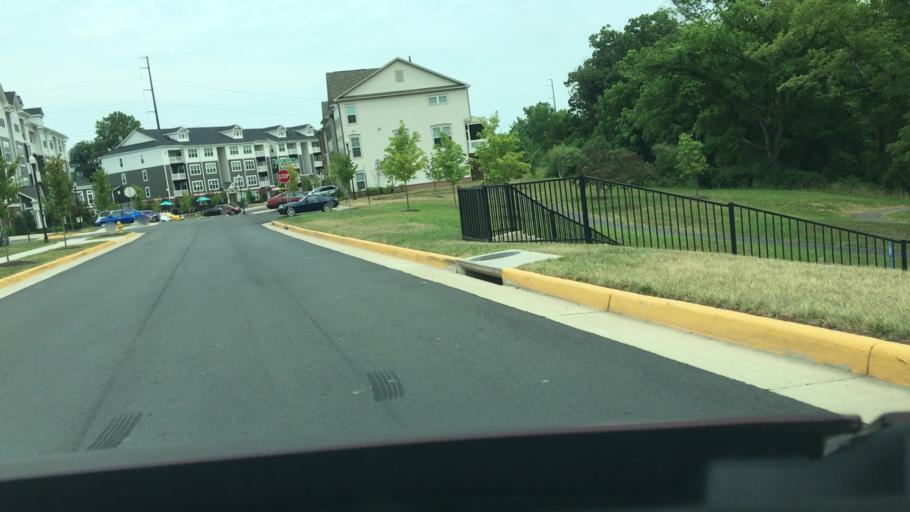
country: US
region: Virginia
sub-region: Prince William County
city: Buckhall
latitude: 38.7602
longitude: -77.4446
